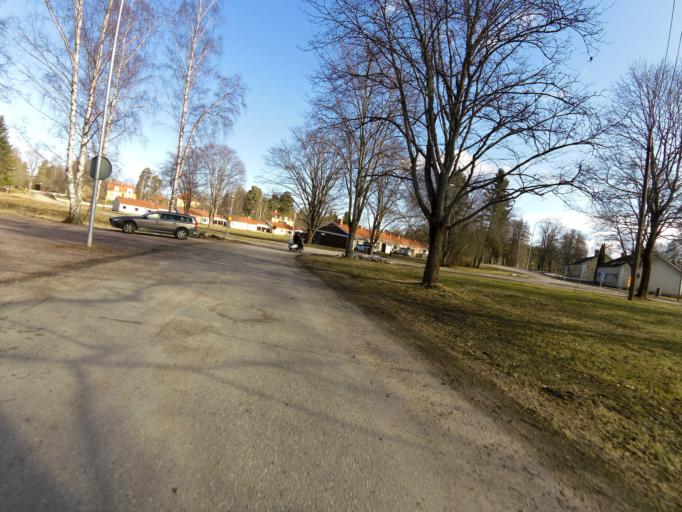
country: SE
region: Gaevleborg
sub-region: Hofors Kommun
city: Hofors
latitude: 60.5554
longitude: 16.2905
